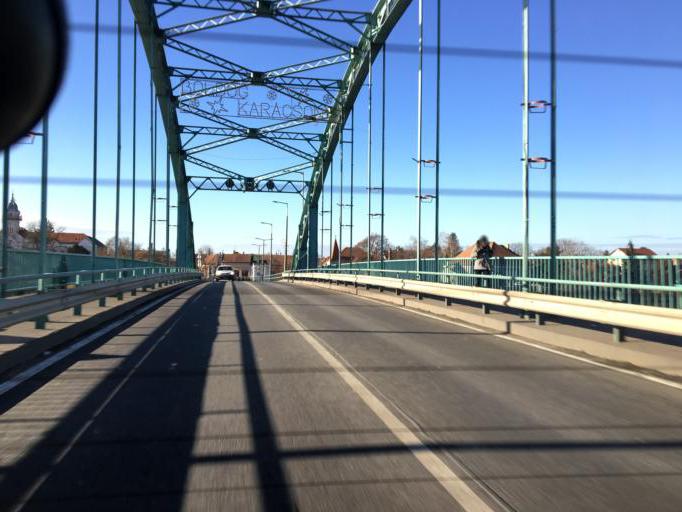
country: HU
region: Pest
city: Rackeve
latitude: 47.1618
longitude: 18.9481
